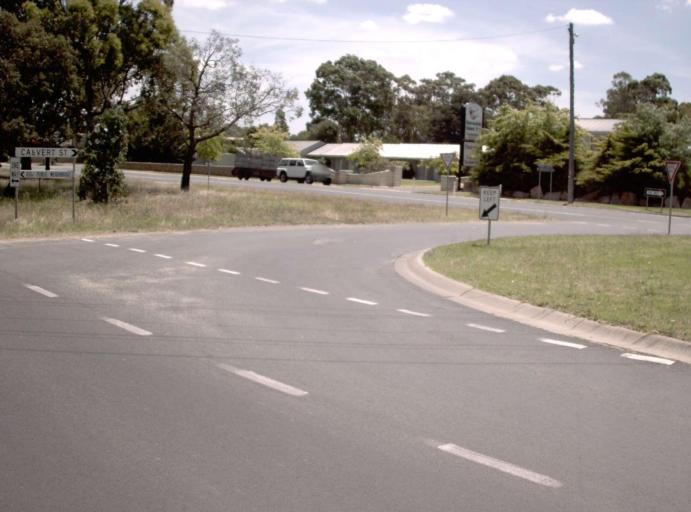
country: AU
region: Victoria
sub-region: East Gippsland
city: Bairnsdale
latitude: -37.8369
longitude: 147.5994
